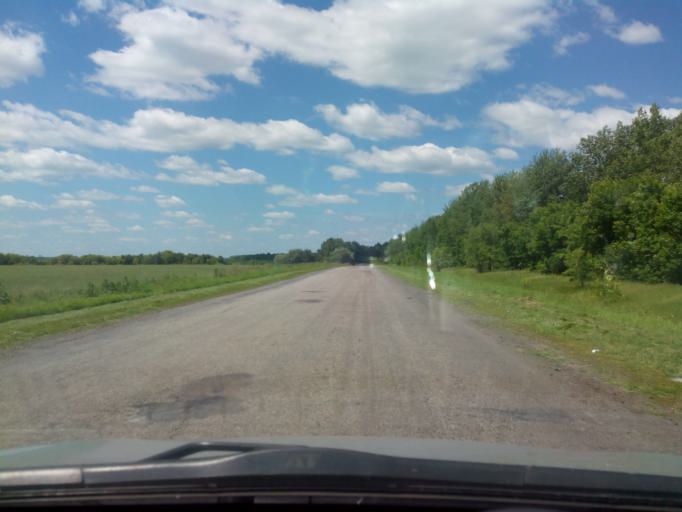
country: RU
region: Voronezj
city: Ternovka
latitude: 51.6329
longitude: 41.7255
